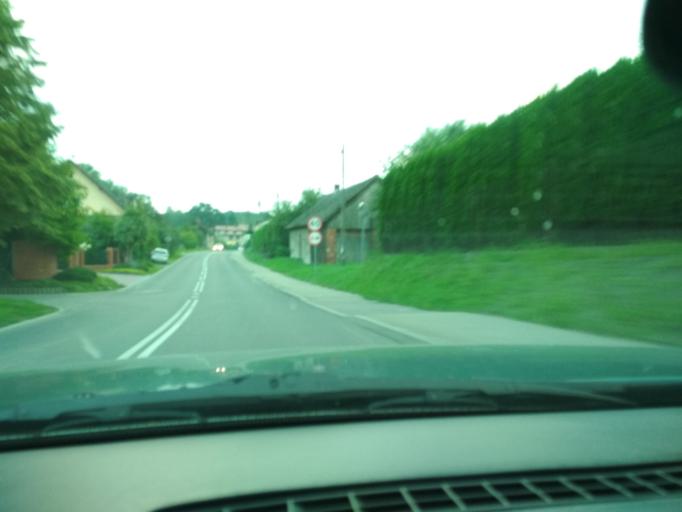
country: PL
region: Silesian Voivodeship
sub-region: Powiat bielski
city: Jasienica
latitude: 49.8403
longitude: 18.9401
